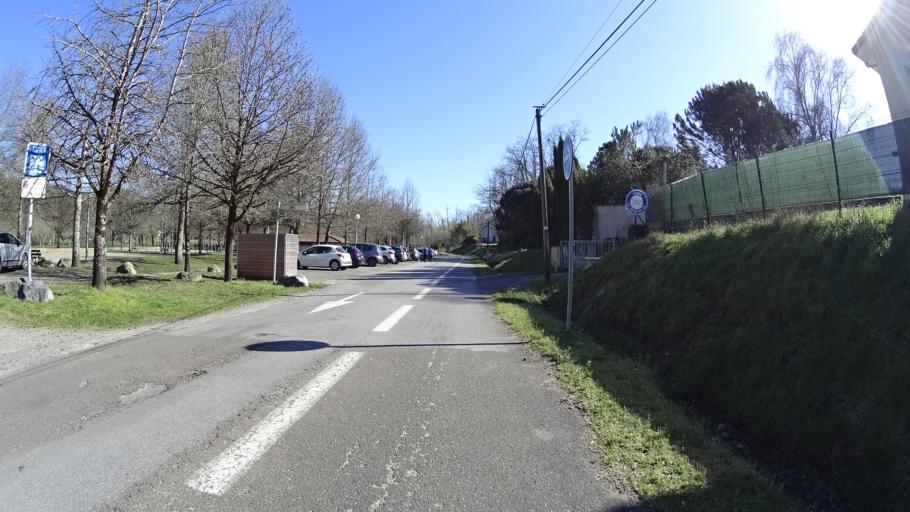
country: FR
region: Aquitaine
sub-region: Departement des Landes
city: Saint-Paul-les-Dax
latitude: 43.7328
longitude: -1.0732
